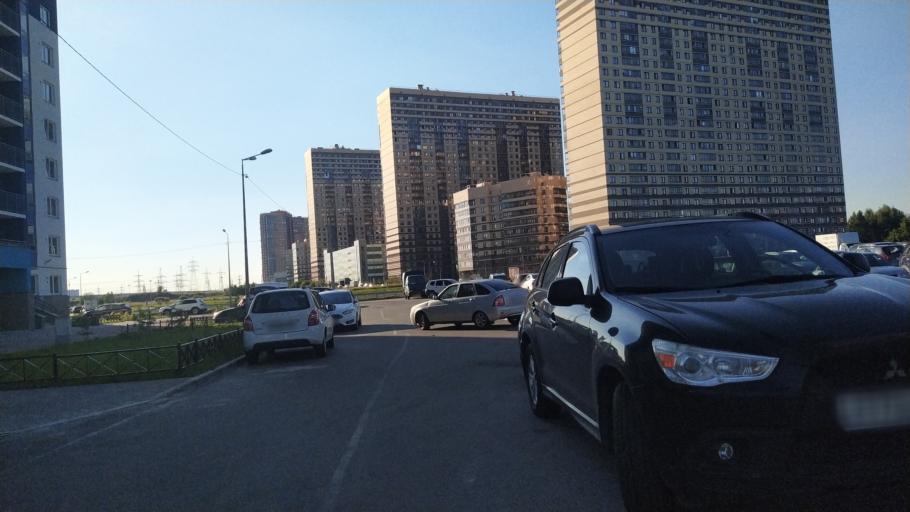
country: RU
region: Leningrad
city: Murino
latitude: 60.0367
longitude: 30.4581
